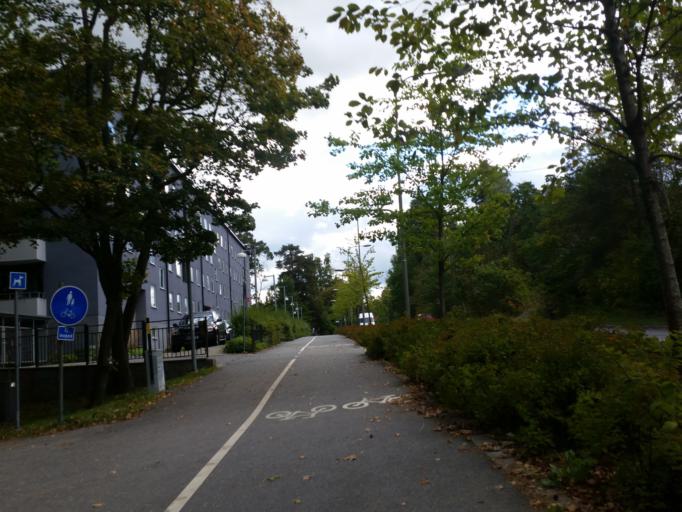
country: SE
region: Stockholm
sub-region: Stockholms Kommun
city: Arsta
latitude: 59.2879
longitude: 18.1011
